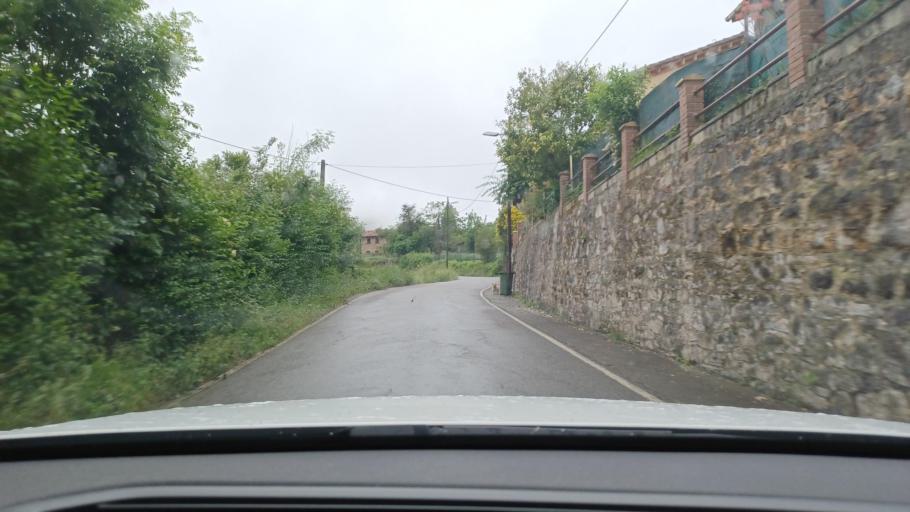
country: ES
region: Asturias
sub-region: Province of Asturias
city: Castandiello
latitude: 43.3037
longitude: -5.9342
